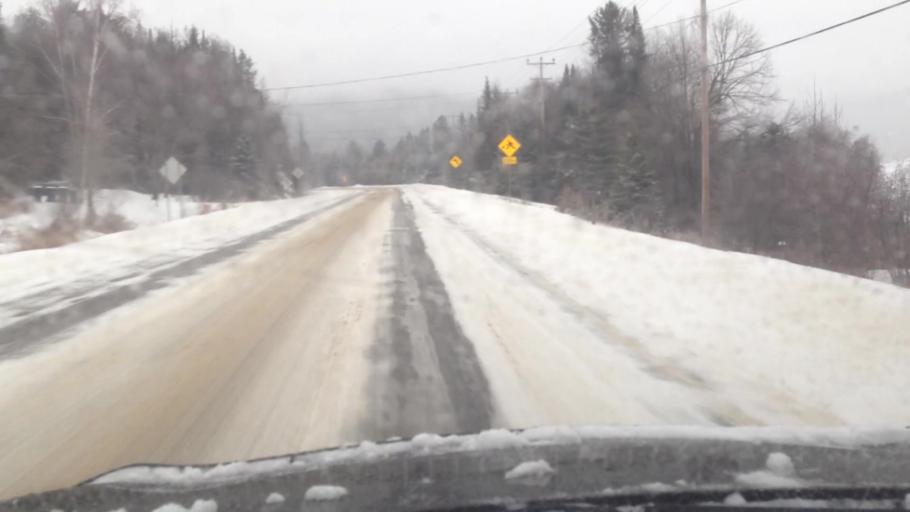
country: CA
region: Quebec
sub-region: Laurentides
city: Mont-Tremblant
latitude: 46.0881
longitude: -74.6095
